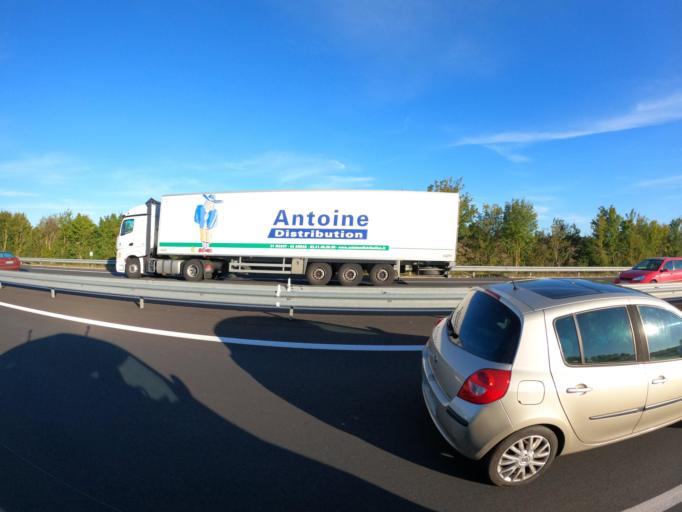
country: FR
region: Pays de la Loire
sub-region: Departement de la Vendee
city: Mortagne-sur-Sevre
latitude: 46.9977
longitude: -0.9106
